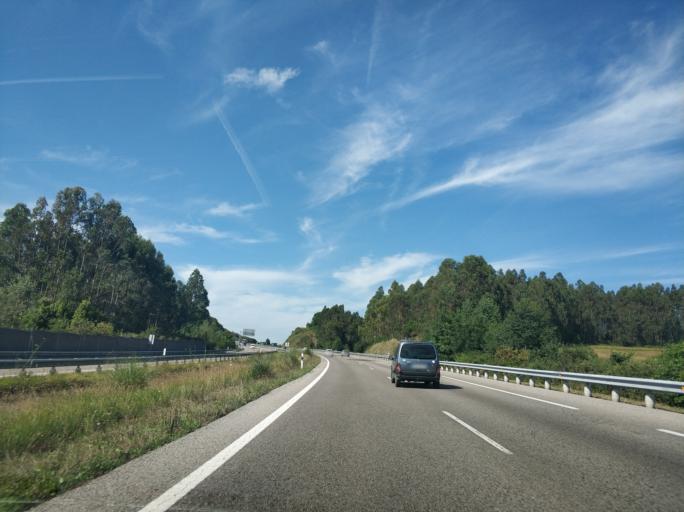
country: ES
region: Asturias
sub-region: Province of Asturias
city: Soto del Barco
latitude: 43.5238
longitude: -6.0571
